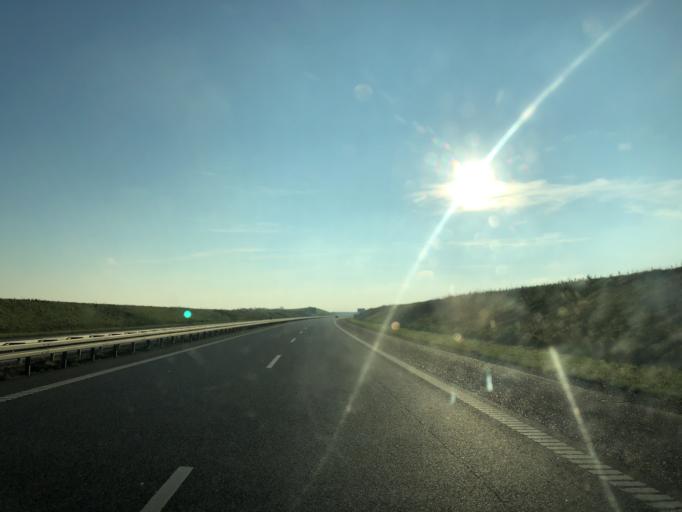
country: DK
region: South Denmark
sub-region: Vejle Kommune
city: Vejle
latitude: 55.7796
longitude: 9.5696
